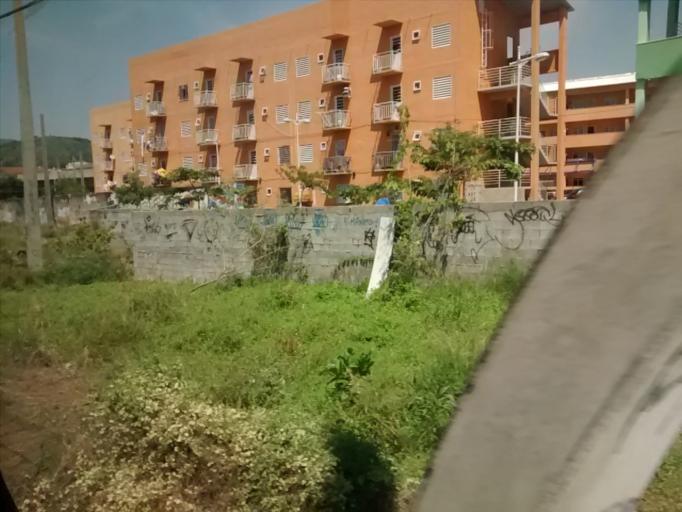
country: BR
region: Rio de Janeiro
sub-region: Rio De Janeiro
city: Rio de Janeiro
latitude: -22.8920
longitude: -43.2464
